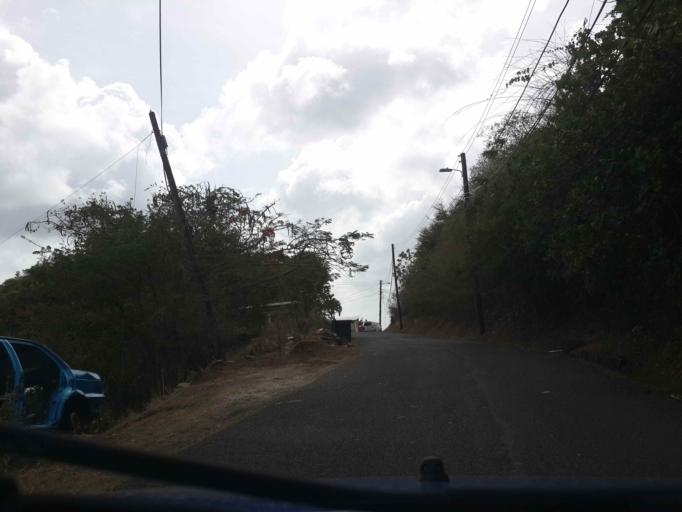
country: LC
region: Castries Quarter
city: Bisee
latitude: 14.0209
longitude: -60.9808
